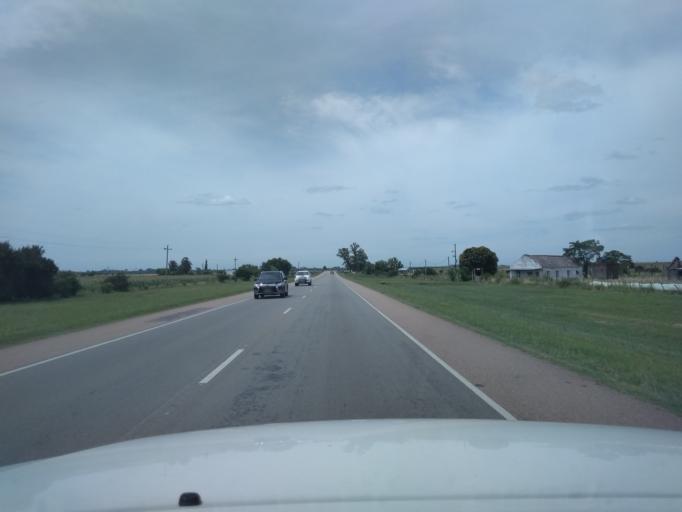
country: UY
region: Canelones
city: Canelones
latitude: -34.3936
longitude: -56.2554
